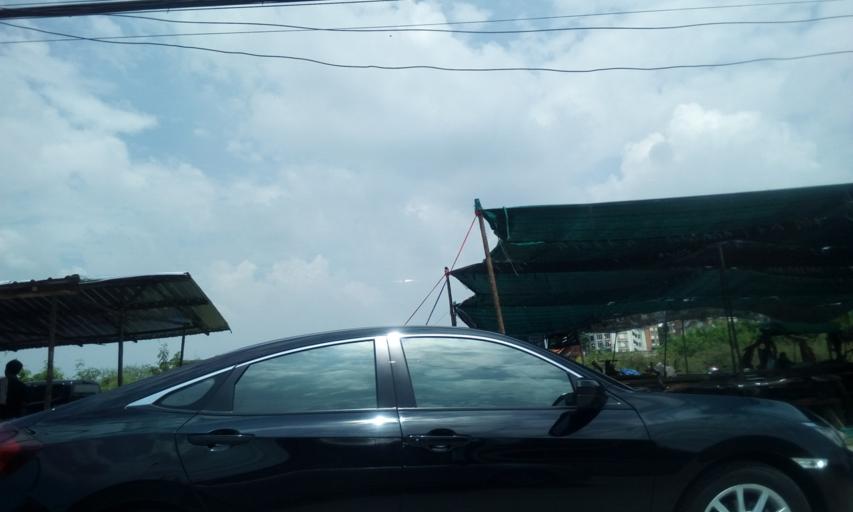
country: TH
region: Nonthaburi
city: Pak Kret
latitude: 13.9392
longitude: 100.5435
